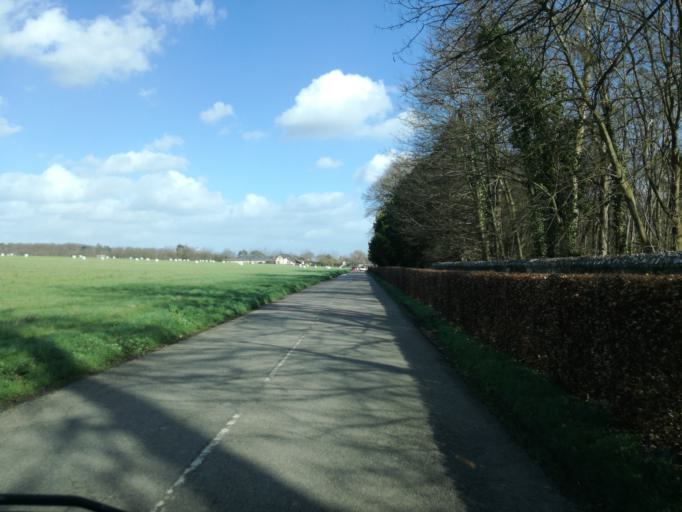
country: FR
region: Haute-Normandie
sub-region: Departement de la Seine-Maritime
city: Sahurs
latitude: 49.3586
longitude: 0.9672
